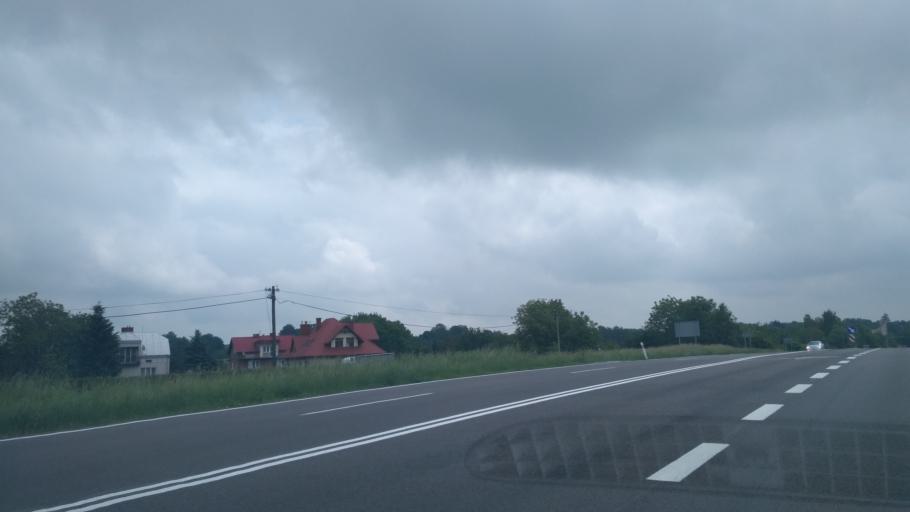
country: PL
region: Subcarpathian Voivodeship
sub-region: Powiat przeworski
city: Rozborz
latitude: 50.0452
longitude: 22.5453
